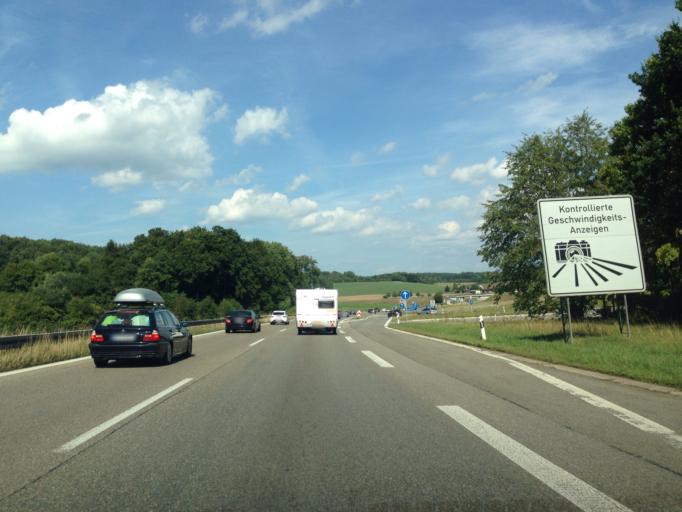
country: DE
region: Baden-Wuerttemberg
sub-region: Regierungsbezirk Stuttgart
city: Hohenstadt
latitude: 48.5451
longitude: 9.6477
